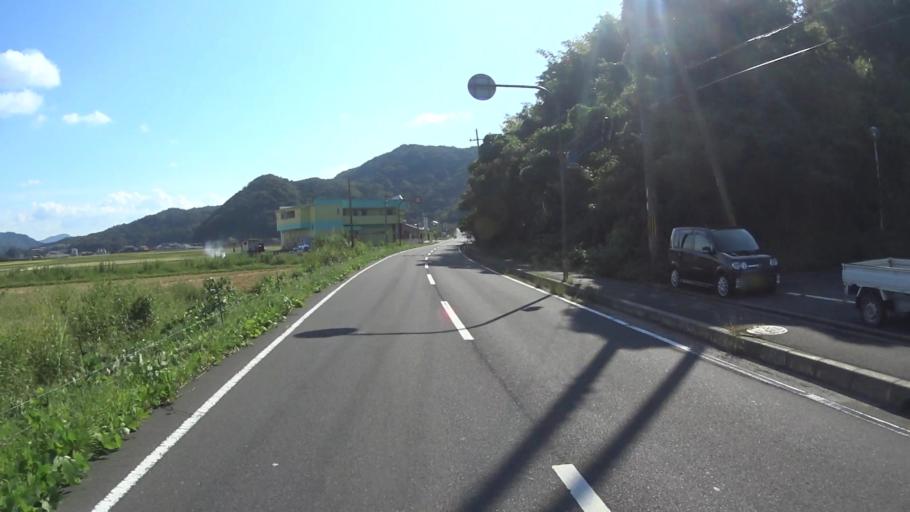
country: JP
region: Kyoto
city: Miyazu
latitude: 35.7360
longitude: 135.0999
